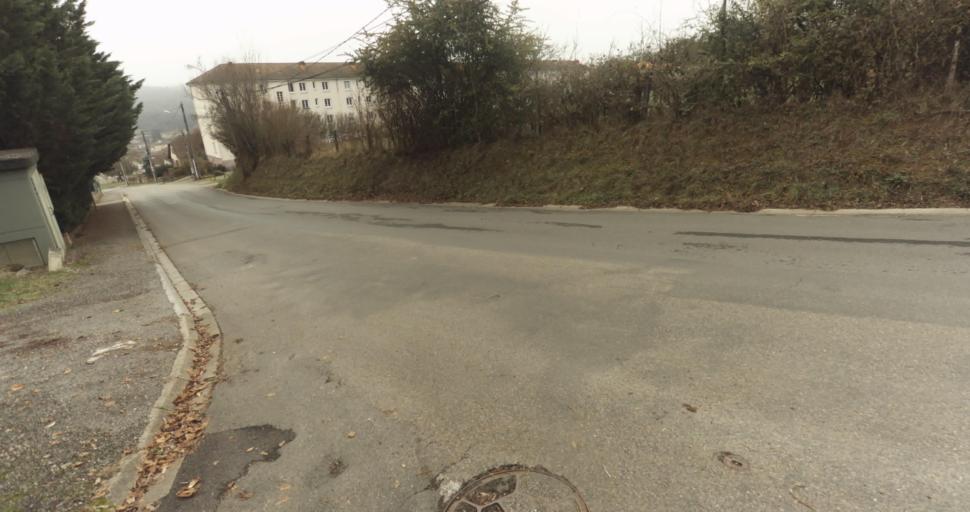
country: FR
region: Midi-Pyrenees
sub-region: Departement du Lot
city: Figeac
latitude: 44.6165
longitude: 2.0256
